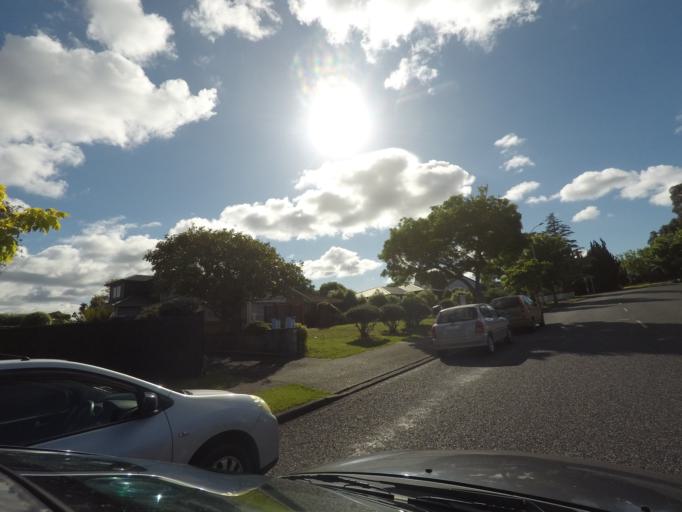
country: NZ
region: Auckland
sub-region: Auckland
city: Manukau City
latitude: -36.9891
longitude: 174.8905
